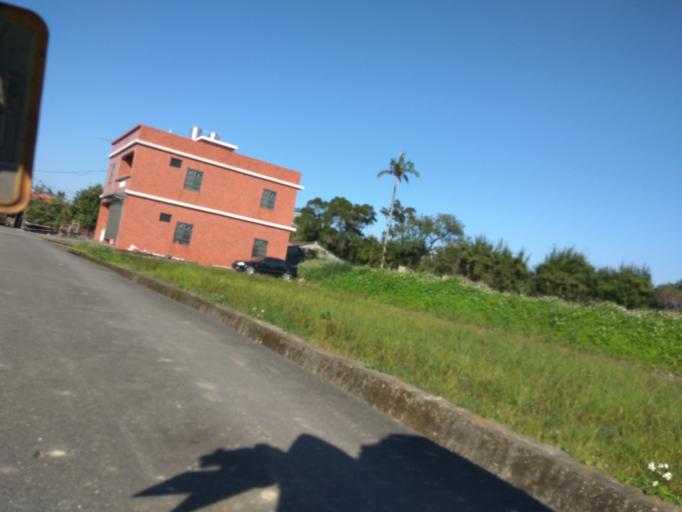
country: TW
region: Taiwan
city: Taoyuan City
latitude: 24.9938
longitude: 121.1988
